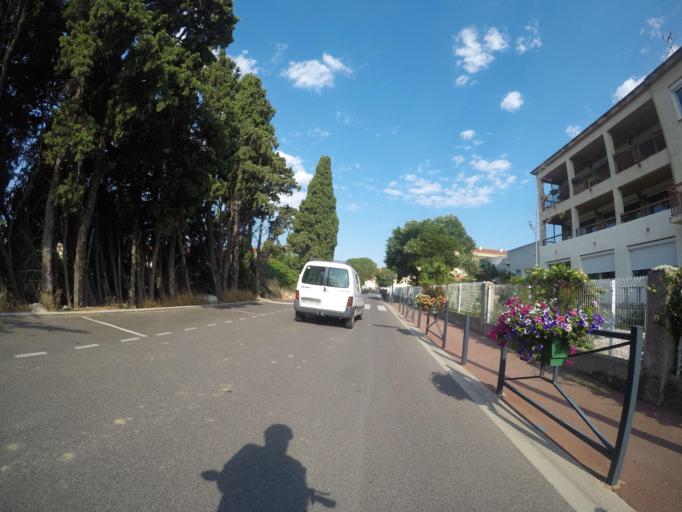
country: FR
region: Languedoc-Roussillon
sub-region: Departement des Pyrenees-Orientales
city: Ille-sur-Tet
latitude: 42.6742
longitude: 2.6280
